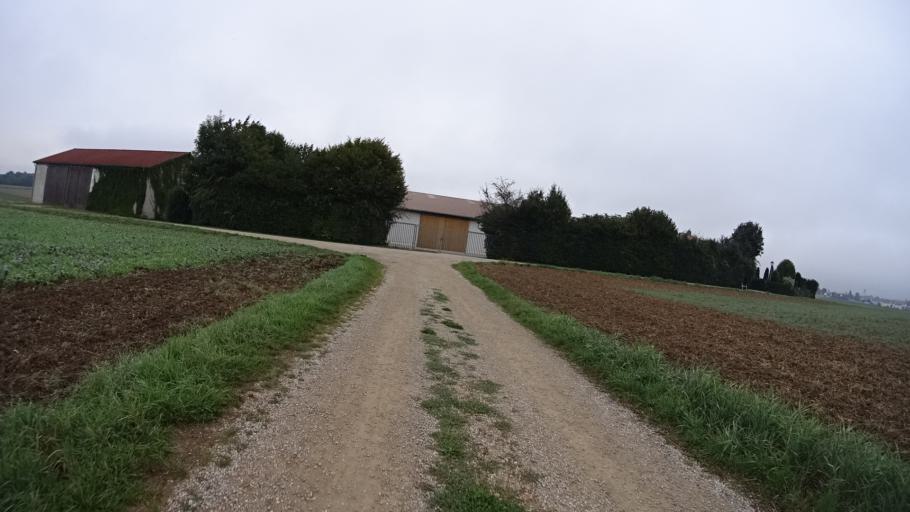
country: DE
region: Bavaria
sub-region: Upper Bavaria
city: Wettstetten
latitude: 48.8157
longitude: 11.3988
